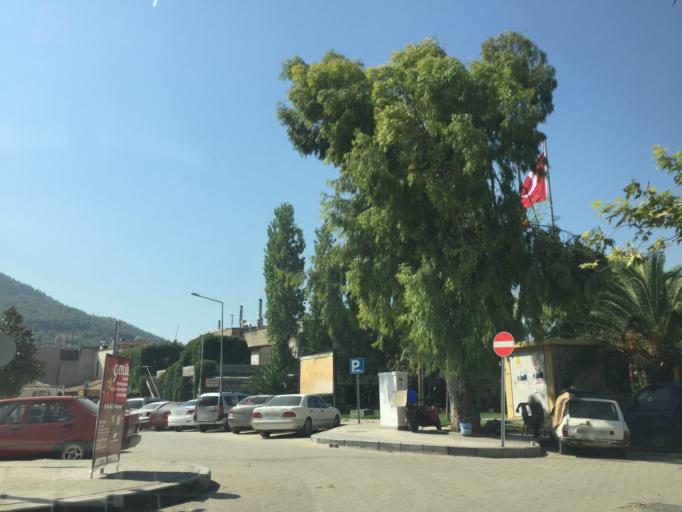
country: TR
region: Izmir
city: Bornova
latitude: 38.4279
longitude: 27.2660
